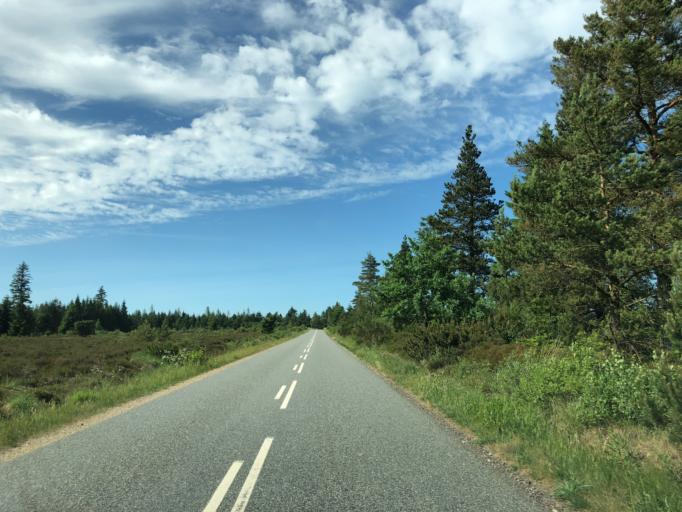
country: DK
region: Central Jutland
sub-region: Herning Kommune
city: Kibaek
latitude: 56.0607
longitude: 8.9186
